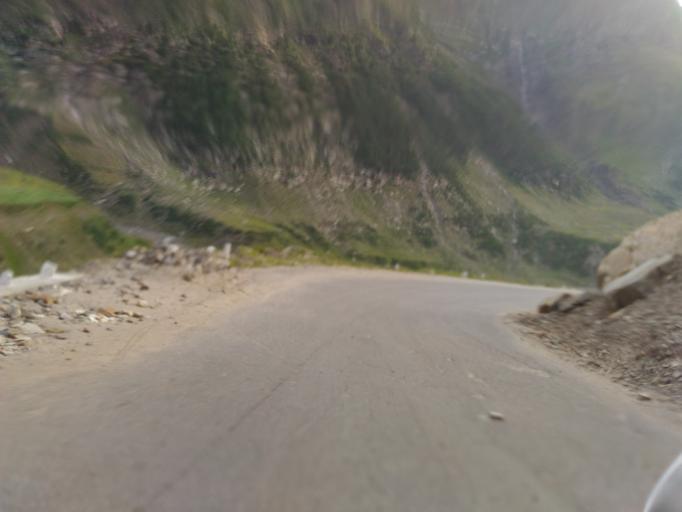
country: IN
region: Himachal Pradesh
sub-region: Kulu
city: Manali
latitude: 32.4364
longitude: 77.1830
